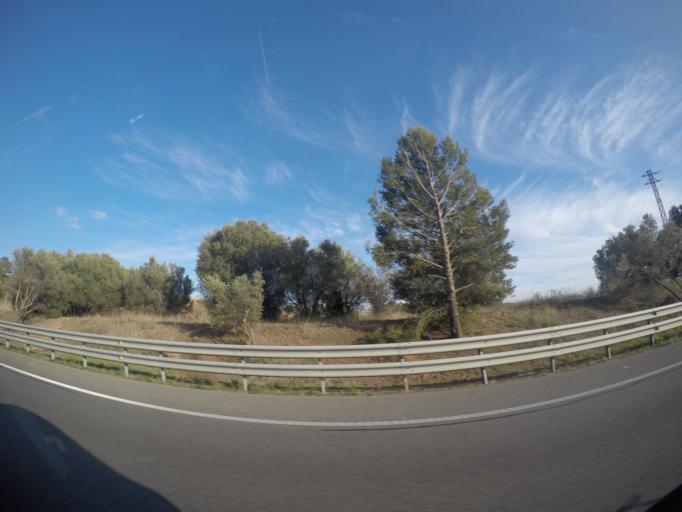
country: ES
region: Catalonia
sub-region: Provincia de Barcelona
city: Castellet
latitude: 41.3218
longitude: 1.6414
